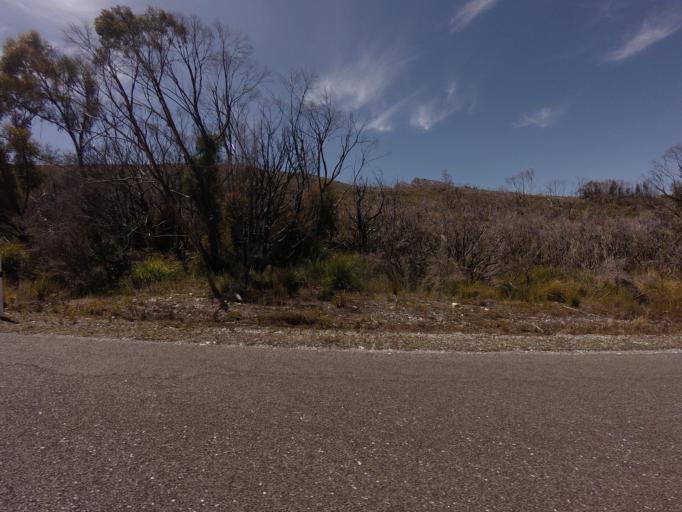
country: AU
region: Tasmania
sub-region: Huon Valley
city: Geeveston
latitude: -42.8371
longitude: 146.1575
